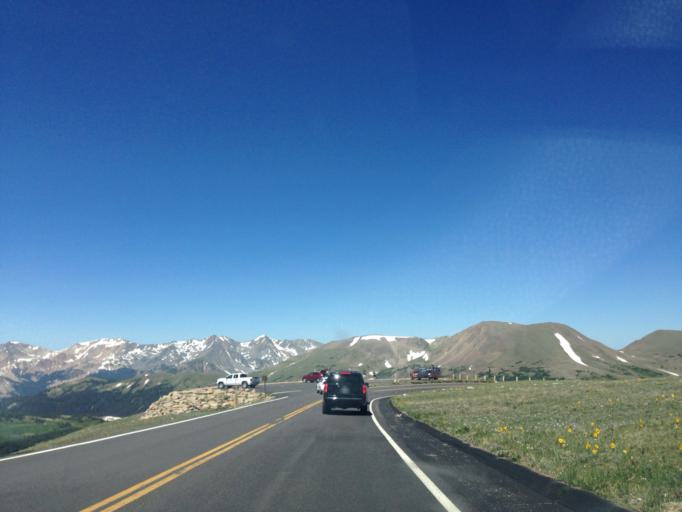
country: US
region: Colorado
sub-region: Larimer County
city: Estes Park
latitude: 40.4325
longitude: -105.7671
